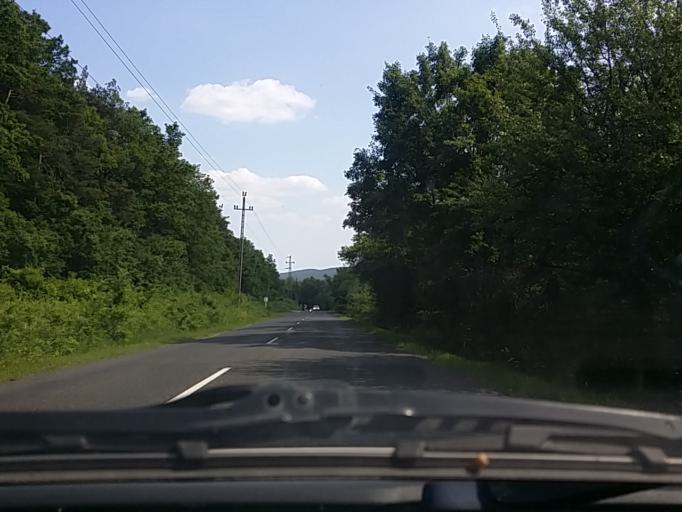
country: HU
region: Pest
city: Pilisszentkereszt
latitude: 47.7021
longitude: 18.8907
